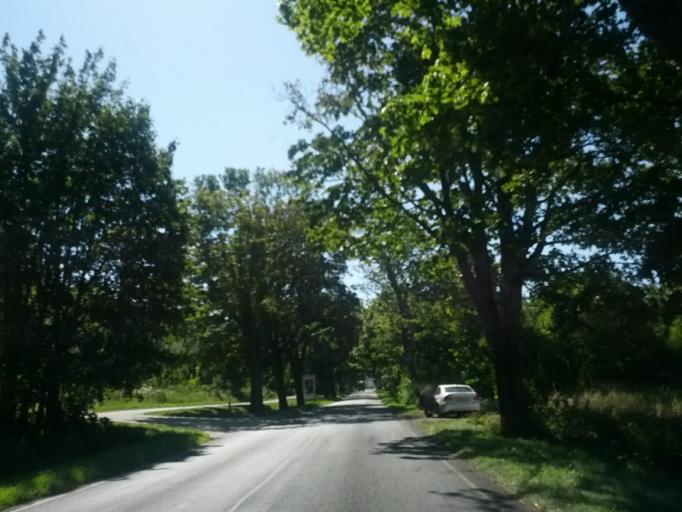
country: DE
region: Mecklenburg-Vorpommern
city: Bergen auf Ruegen
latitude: 54.4259
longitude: 13.4326
